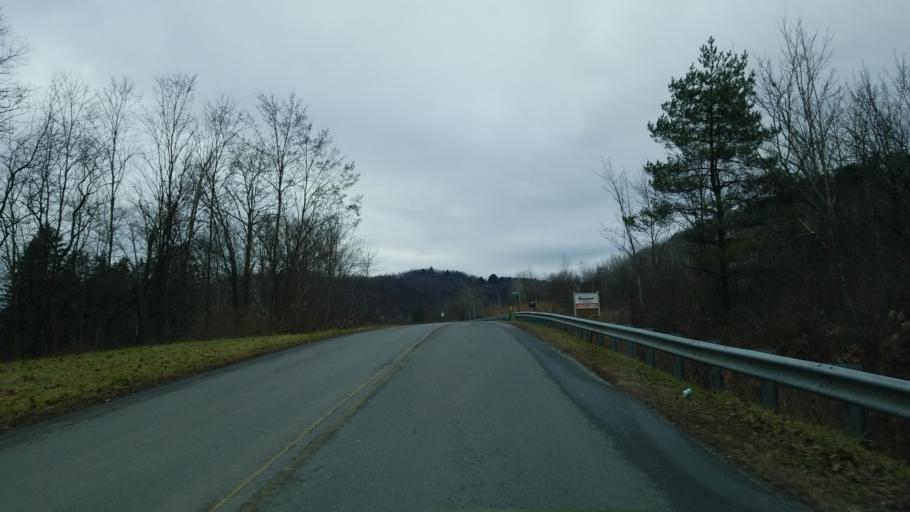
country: US
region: Pennsylvania
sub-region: Clearfield County
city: Clearfield
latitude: 41.0352
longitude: -78.4332
